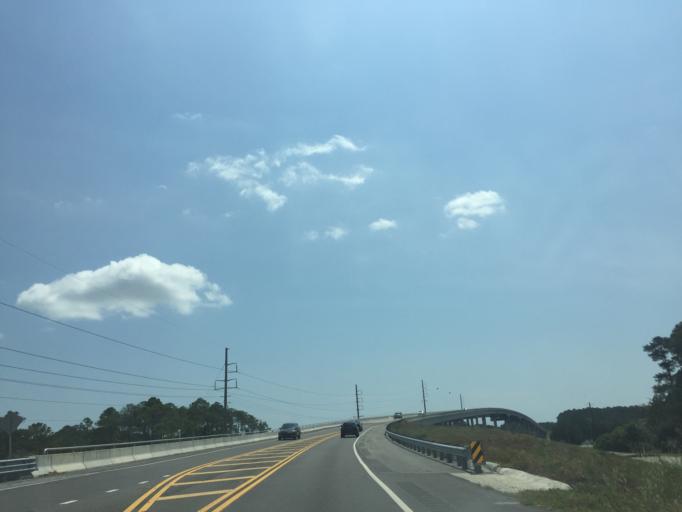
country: US
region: Georgia
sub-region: Chatham County
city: Skidaway Island
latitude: 31.9499
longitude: -81.0697
